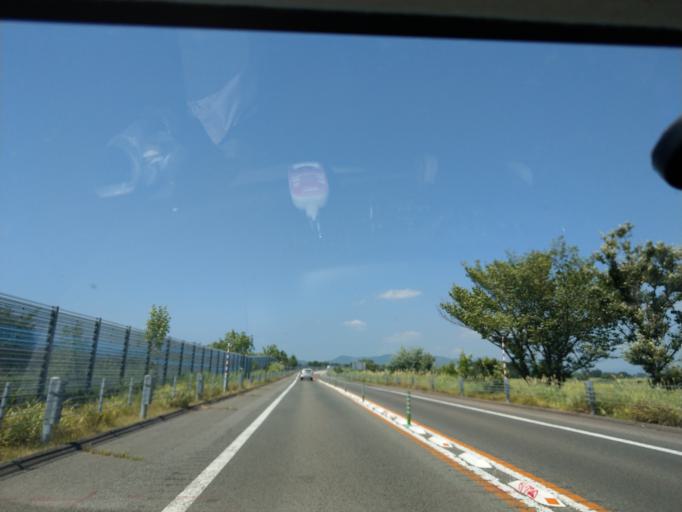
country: JP
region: Akita
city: Yokotemachi
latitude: 39.3550
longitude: 140.4943
